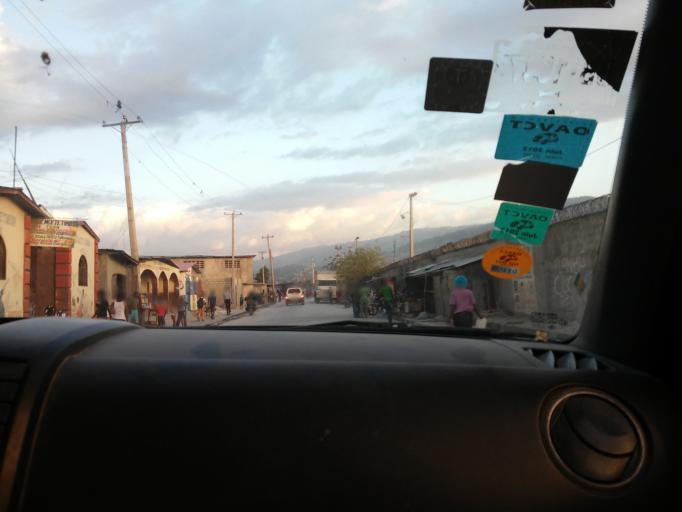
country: HT
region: Ouest
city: Port-au-Prince
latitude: 18.5651
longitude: -72.3460
